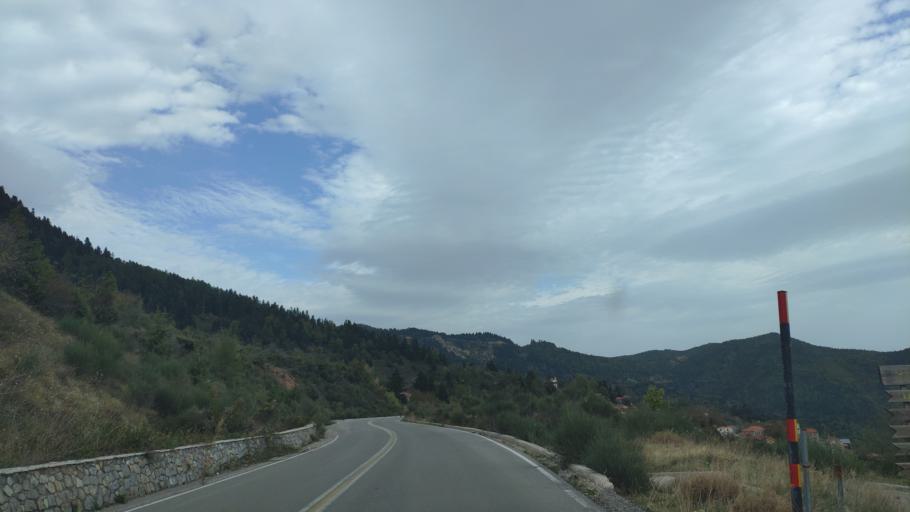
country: GR
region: Central Greece
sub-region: Nomos Fokidos
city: Amfissa
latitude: 38.6839
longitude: 22.3195
